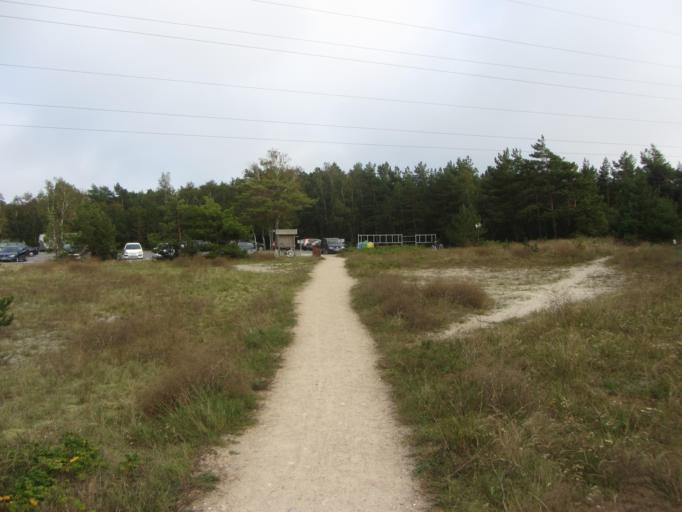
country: LT
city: Neringa
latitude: 55.4210
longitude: 21.0594
